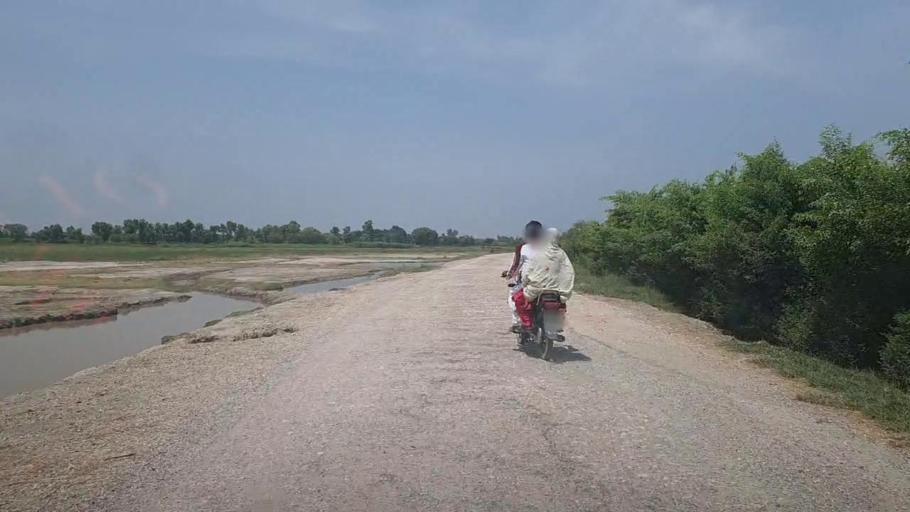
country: PK
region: Sindh
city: Ubauro
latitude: 28.1863
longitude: 69.7695
